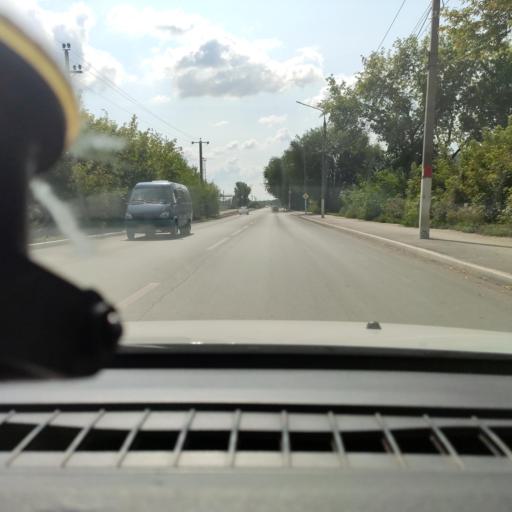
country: RU
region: Samara
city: Chapayevsk
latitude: 52.9810
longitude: 49.7051
